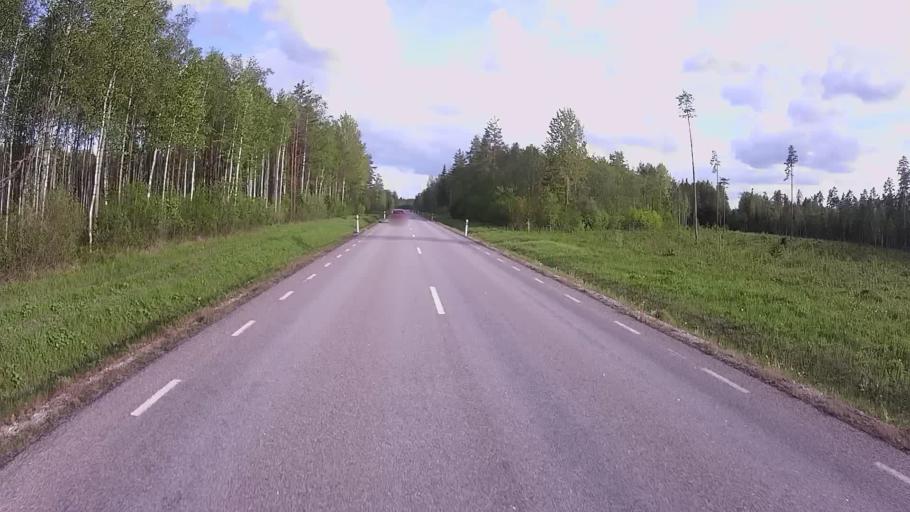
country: EE
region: Jogevamaa
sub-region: Mustvee linn
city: Mustvee
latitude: 59.0699
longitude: 26.9990
